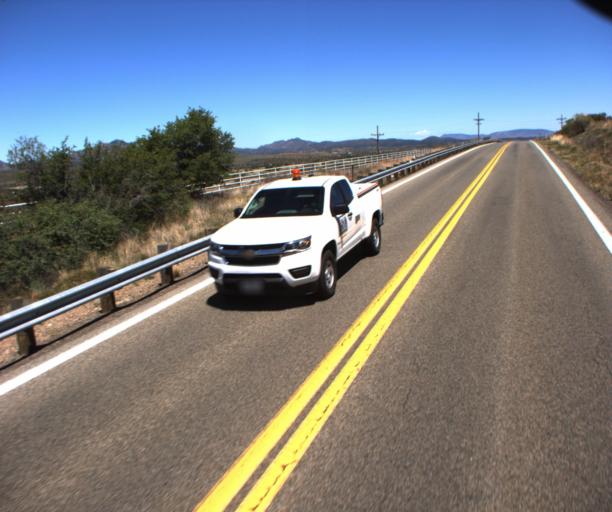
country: US
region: Arizona
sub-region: Yavapai County
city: Congress
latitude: 34.2432
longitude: -112.7365
